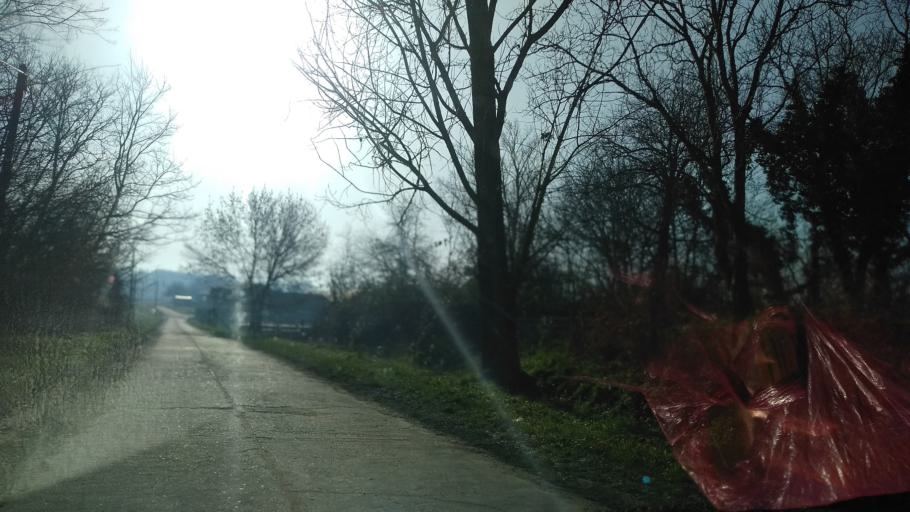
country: HU
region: Somogy
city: Barcs
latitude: 45.9546
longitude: 17.4873
